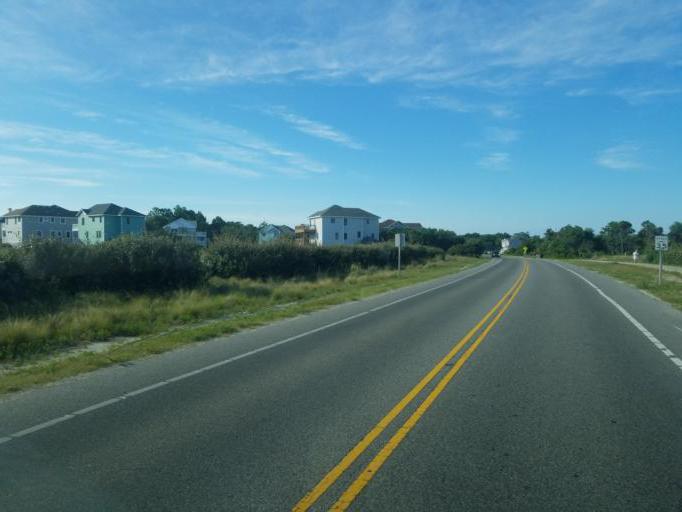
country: US
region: North Carolina
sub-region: Currituck County
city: Currituck
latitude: 36.3850
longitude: -75.8309
